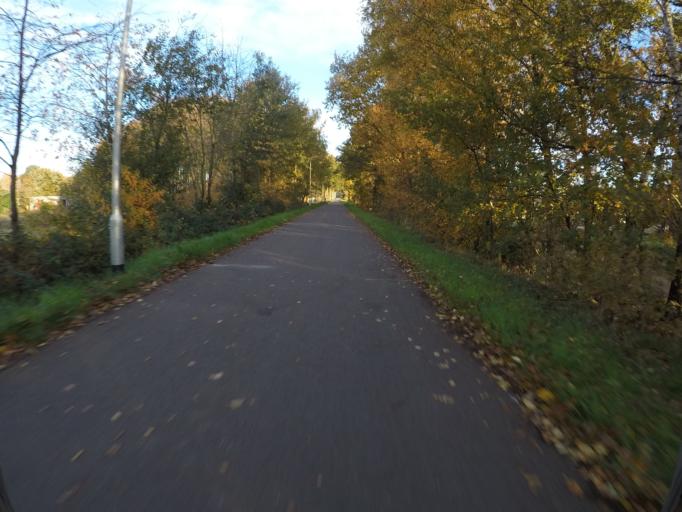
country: BE
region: Flanders
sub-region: Provincie Antwerpen
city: Herentals
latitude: 51.1528
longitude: 4.8205
